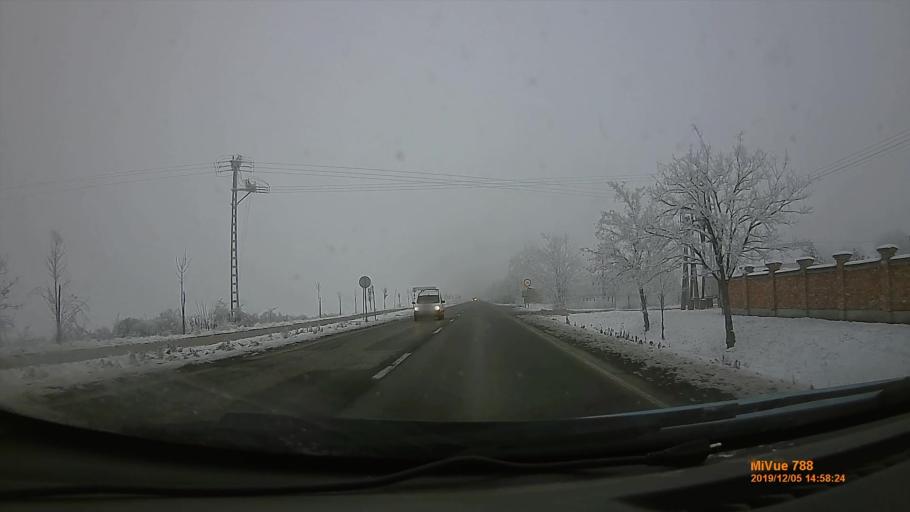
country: HU
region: Szabolcs-Szatmar-Bereg
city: Nyirtelek
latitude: 48.0481
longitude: 21.5721
